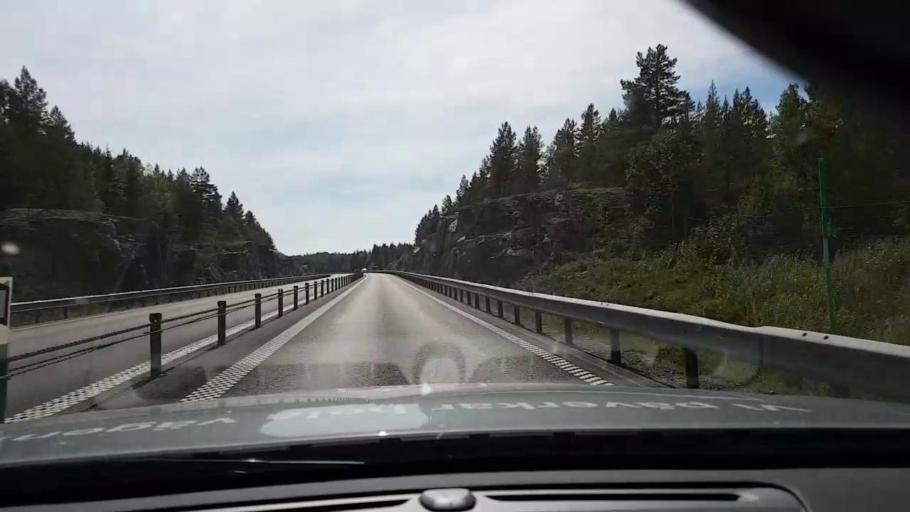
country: SE
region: Vaesternorrland
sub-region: OErnskoeldsviks Kommun
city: Husum
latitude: 63.3970
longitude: 19.1974
